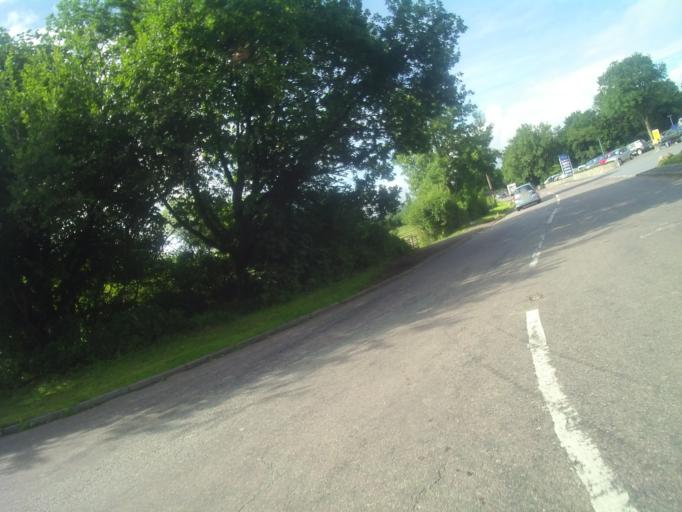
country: GB
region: England
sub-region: Devon
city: Ashburton
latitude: 50.5098
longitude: -3.7633
